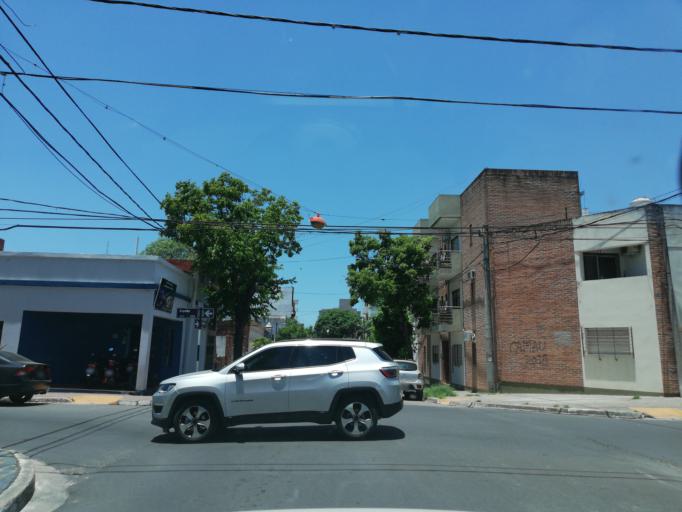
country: AR
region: Corrientes
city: Corrientes
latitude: -27.4650
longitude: -58.8289
